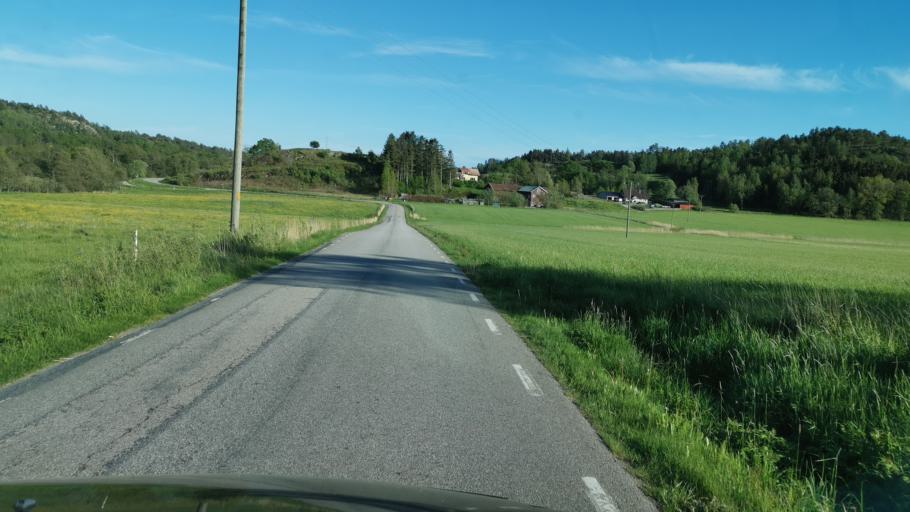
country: SE
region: Vaestra Goetaland
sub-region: Orust
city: Henan
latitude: 58.2774
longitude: 11.5946
